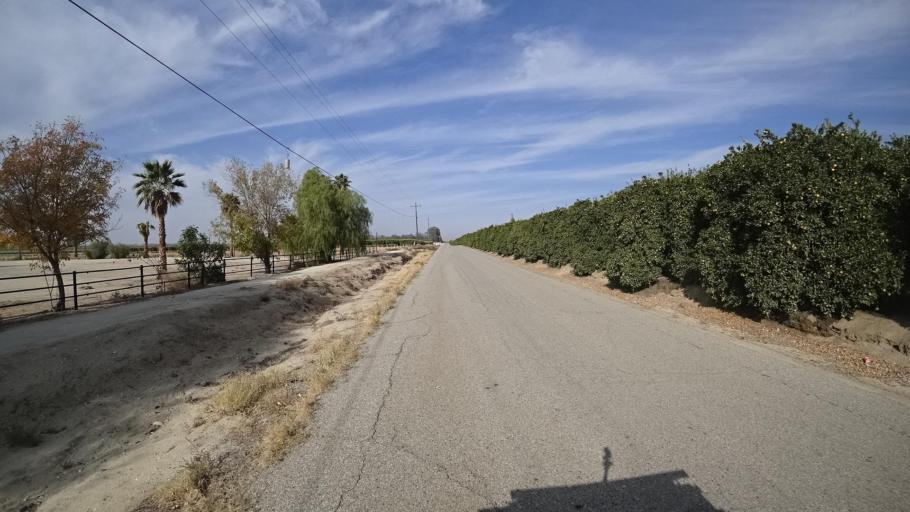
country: US
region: California
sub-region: Kern County
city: Arvin
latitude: 35.2772
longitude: -118.7527
